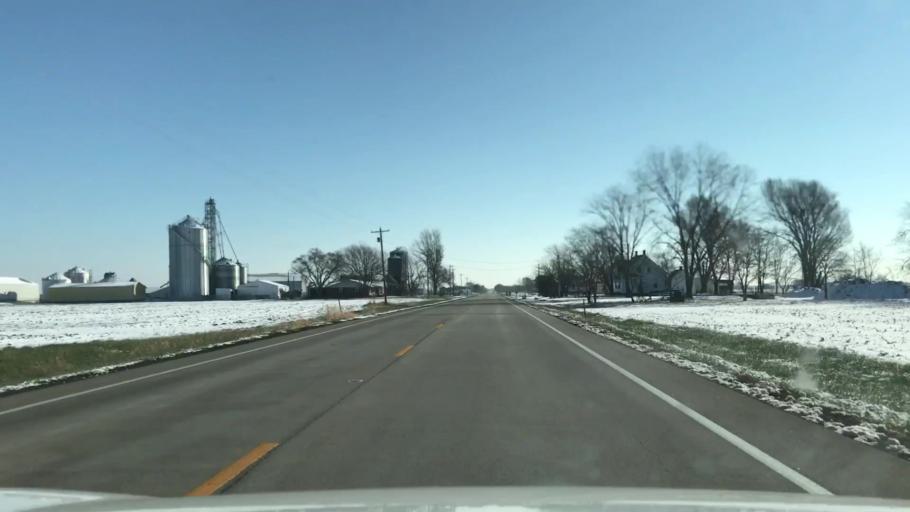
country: US
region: Illinois
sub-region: Washington County
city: Okawville
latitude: 38.4422
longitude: -89.4901
